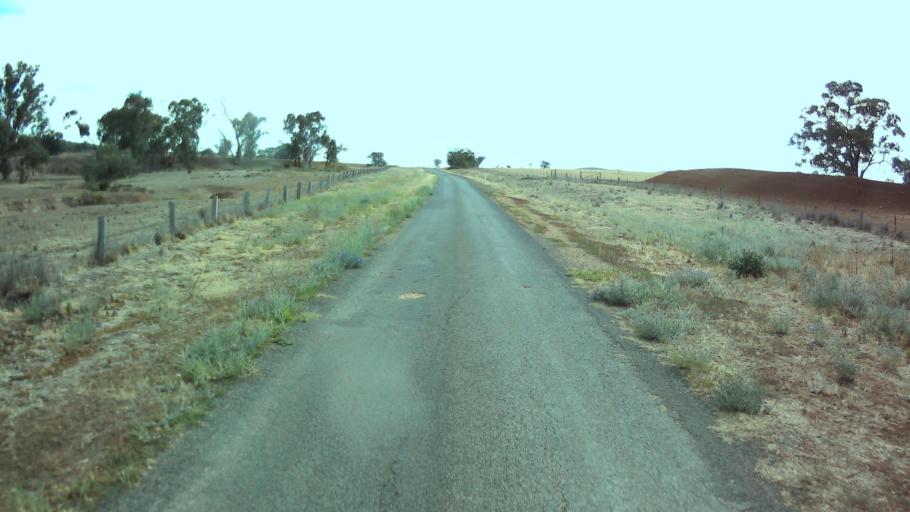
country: AU
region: New South Wales
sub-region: Weddin
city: Grenfell
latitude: -33.8384
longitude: 148.2661
